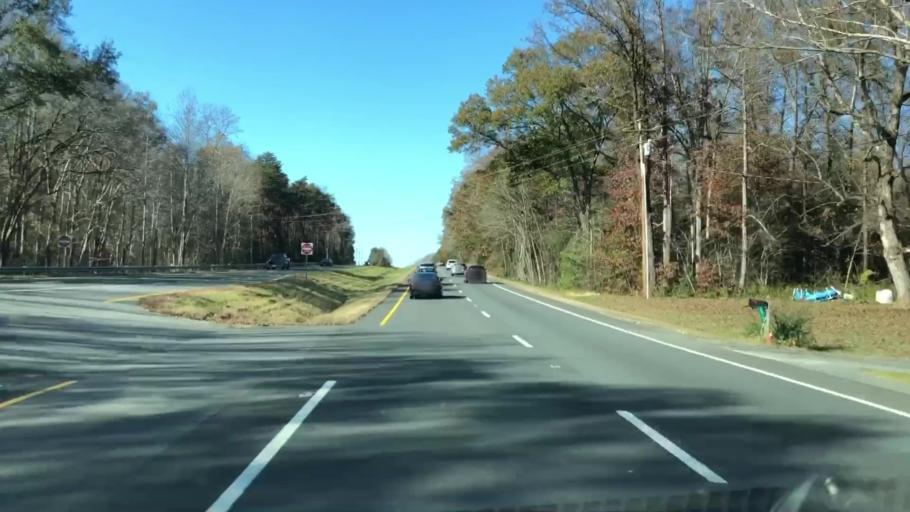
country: US
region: Virginia
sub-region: Fauquier County
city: Bealeton
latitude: 38.4624
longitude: -77.6702
